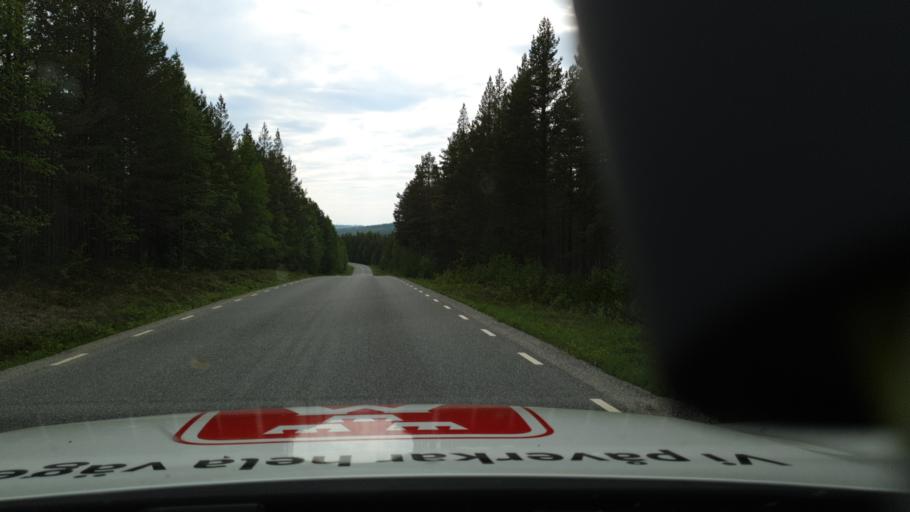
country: SE
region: Jaemtland
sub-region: Braecke Kommun
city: Braecke
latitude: 63.1035
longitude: 15.4517
